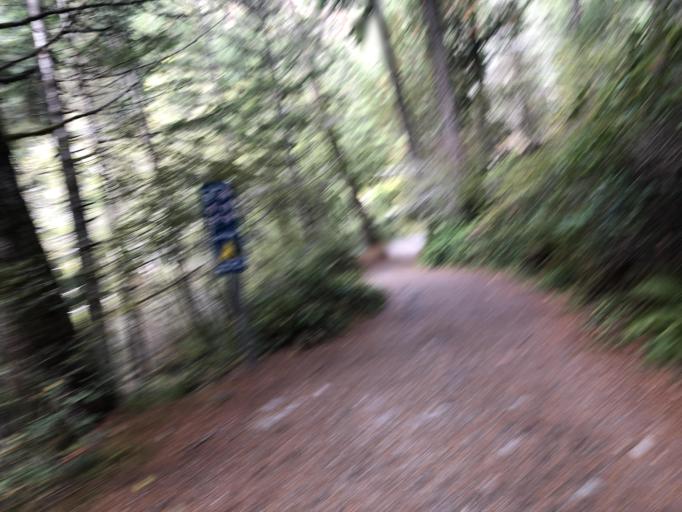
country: CA
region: British Columbia
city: Sooke
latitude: 48.4316
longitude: -123.7142
